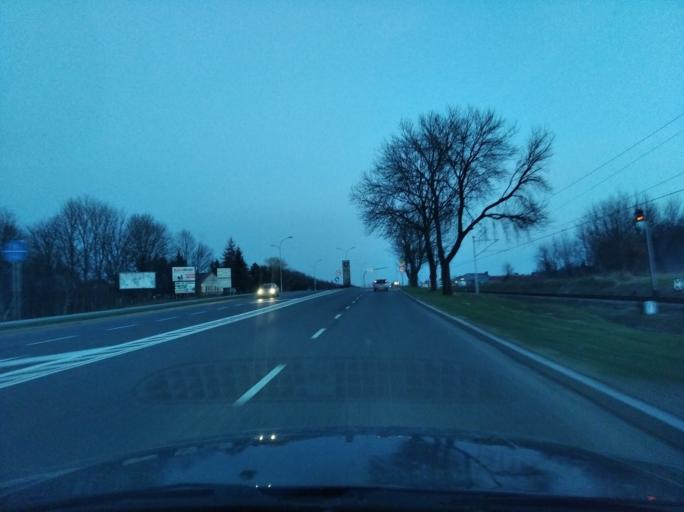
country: PL
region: Subcarpathian Voivodeship
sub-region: Rzeszow
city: Rzeszow
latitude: 50.0736
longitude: 21.9883
